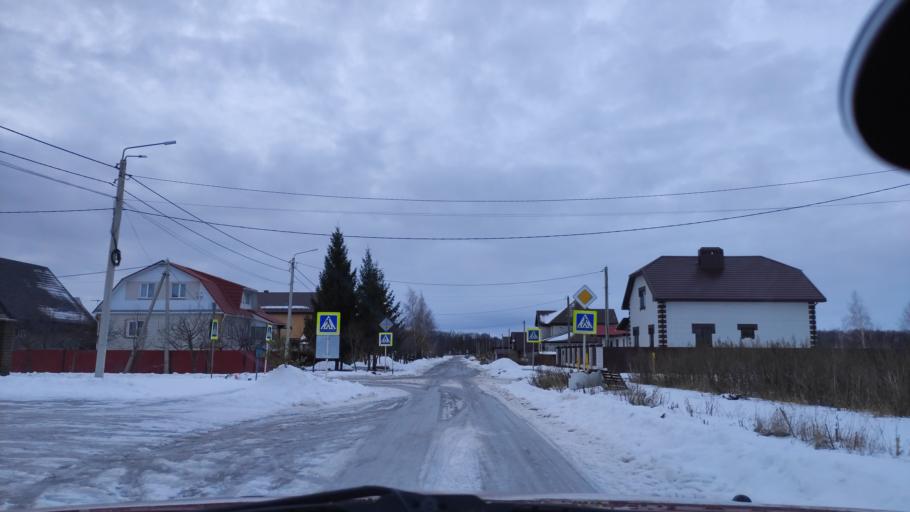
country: RU
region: Tambov
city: Komsomolets
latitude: 52.7642
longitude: 41.3614
